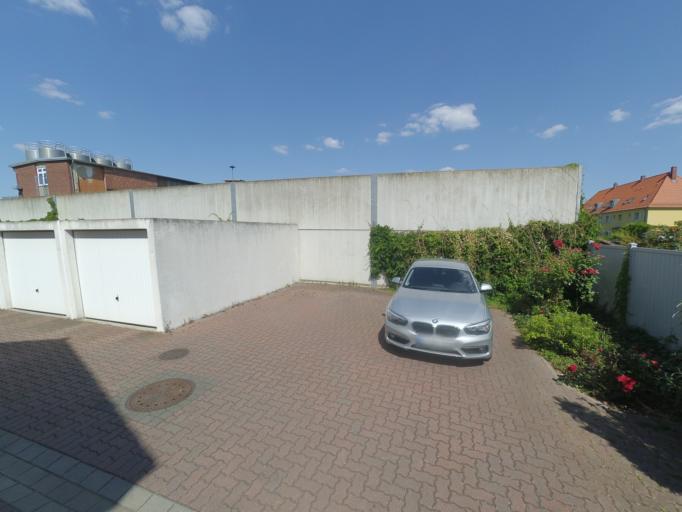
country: DE
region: Rheinland-Pfalz
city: Frankenthal
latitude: 49.5282
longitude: 8.3565
